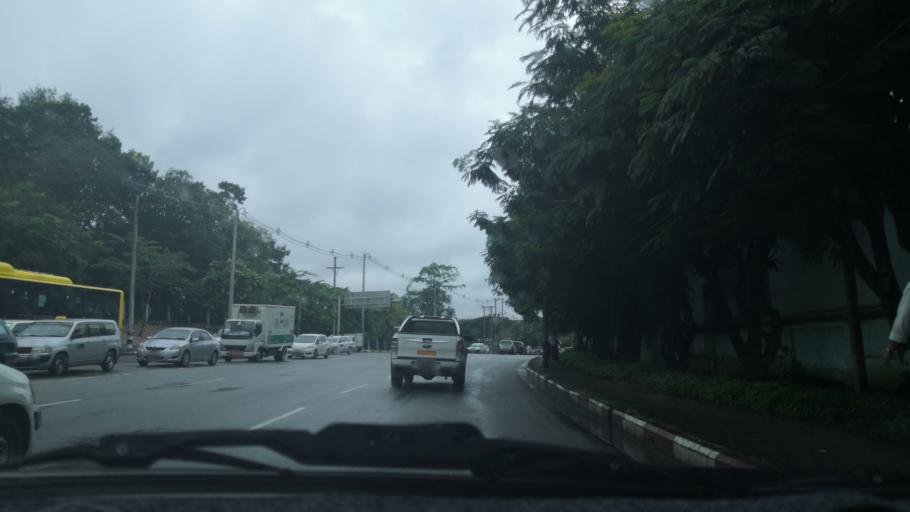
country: MM
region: Yangon
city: Yangon
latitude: 16.8905
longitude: 96.1206
